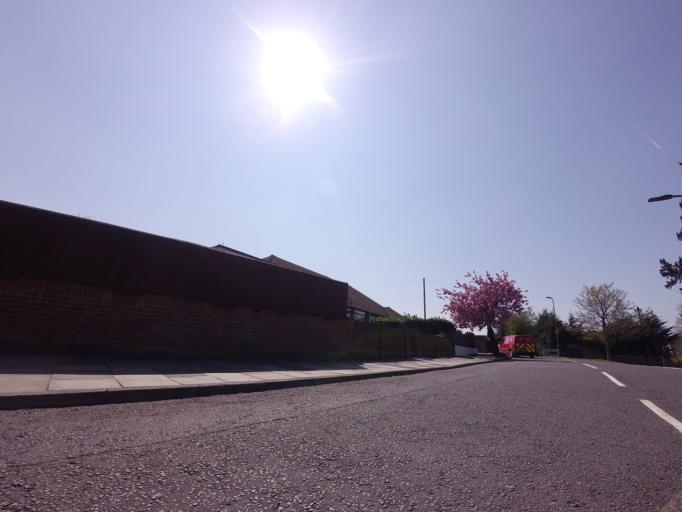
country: GB
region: England
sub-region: Greater London
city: Orpington
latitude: 51.3833
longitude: 0.1108
